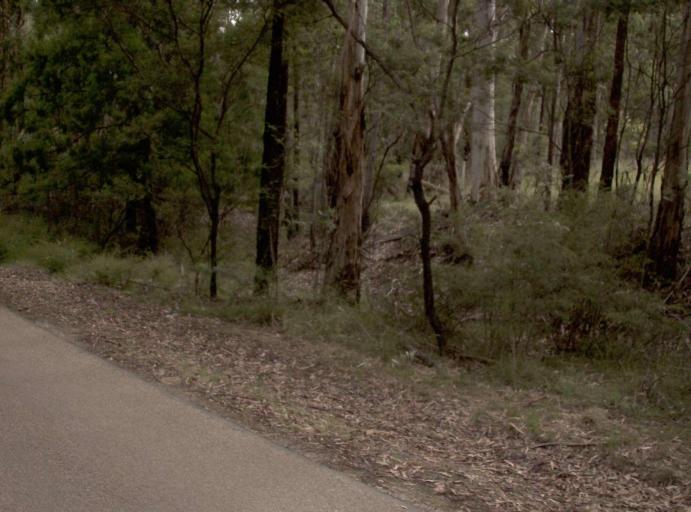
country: AU
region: Victoria
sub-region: East Gippsland
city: Bairnsdale
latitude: -37.7108
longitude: 147.5924
